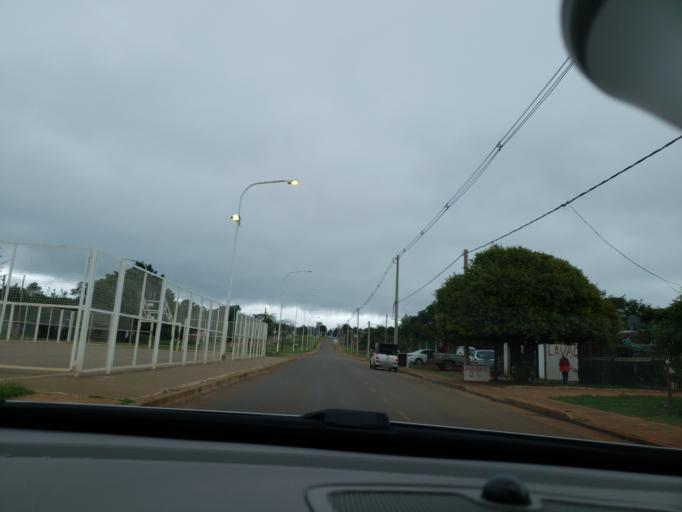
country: AR
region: Misiones
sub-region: Departamento de Capital
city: Posadas
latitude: -27.4252
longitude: -55.8760
